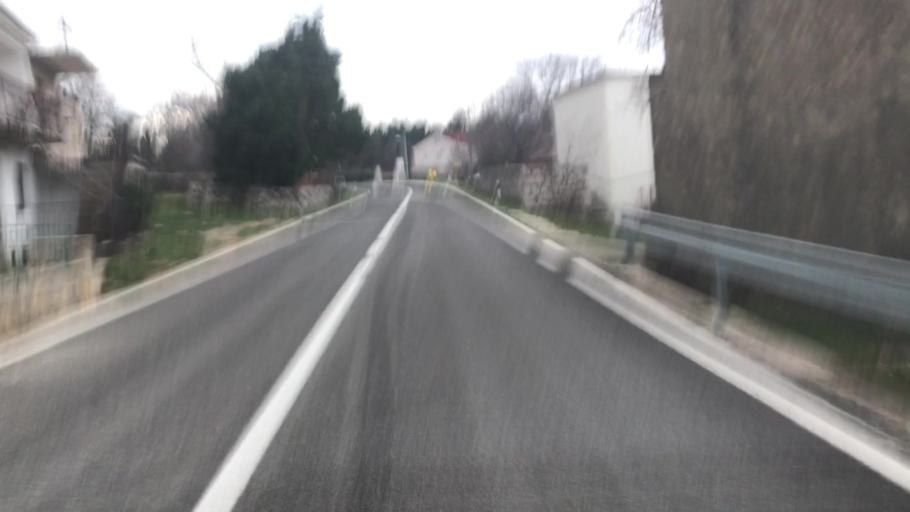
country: HR
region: Zadarska
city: Razanac
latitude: 44.3396
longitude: 15.3389
